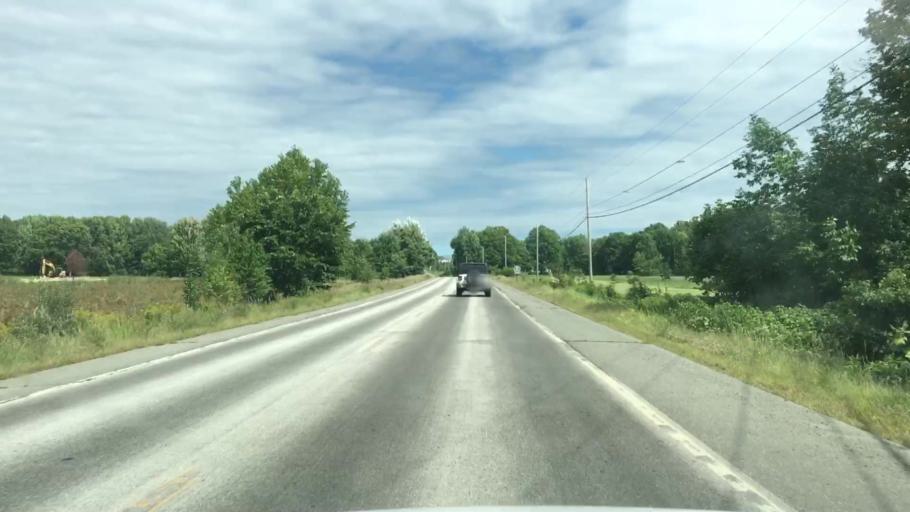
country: US
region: Maine
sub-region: Piscataquis County
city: Dover-Foxcroft
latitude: 45.1564
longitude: -69.2345
